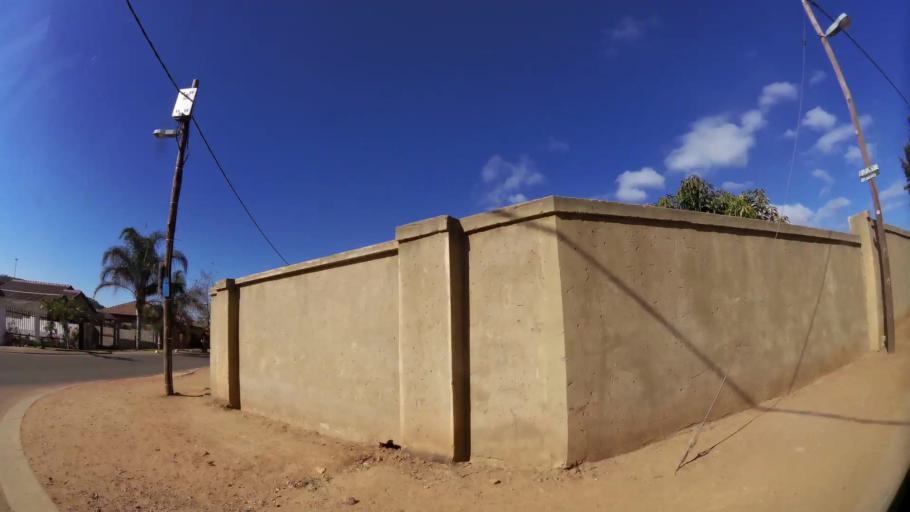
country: ZA
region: Gauteng
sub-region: City of Tshwane Metropolitan Municipality
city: Cullinan
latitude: -25.6893
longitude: 28.4134
